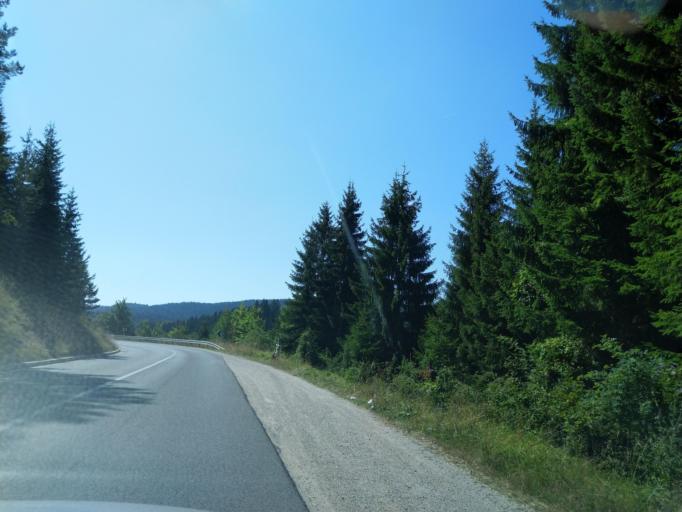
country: RS
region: Central Serbia
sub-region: Zlatiborski Okrug
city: Nova Varos
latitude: 43.4347
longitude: 19.8242
